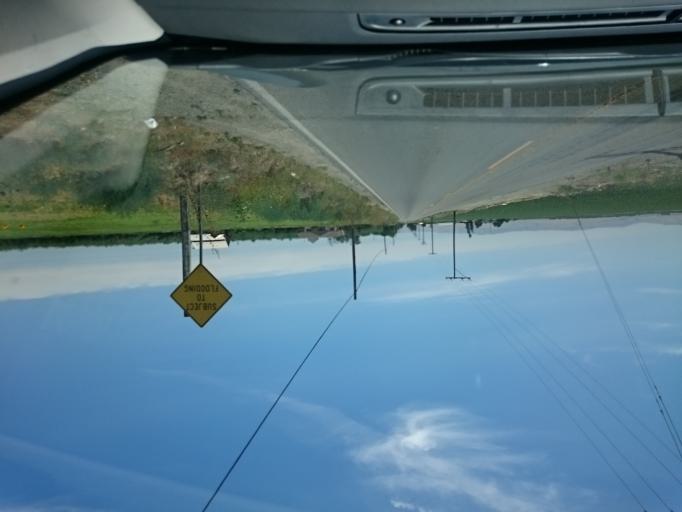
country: US
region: California
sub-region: Stanislaus County
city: Bret Harte
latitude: 37.5513
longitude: -120.9942
